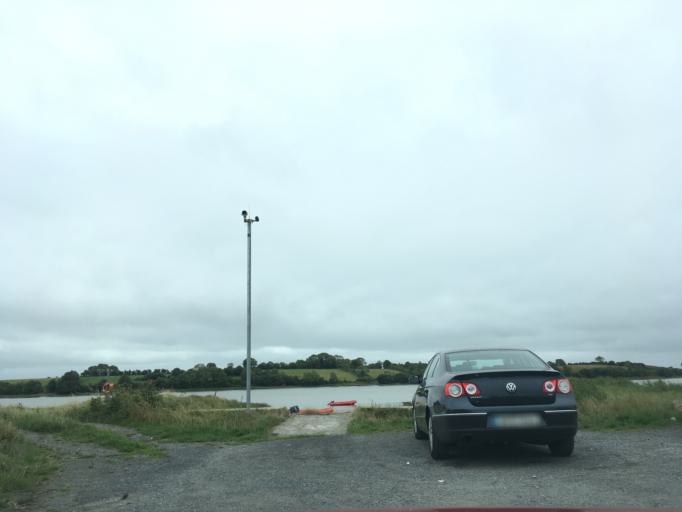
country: IE
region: Munster
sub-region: County Limerick
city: Askeaton
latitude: 52.7159
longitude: -9.0544
